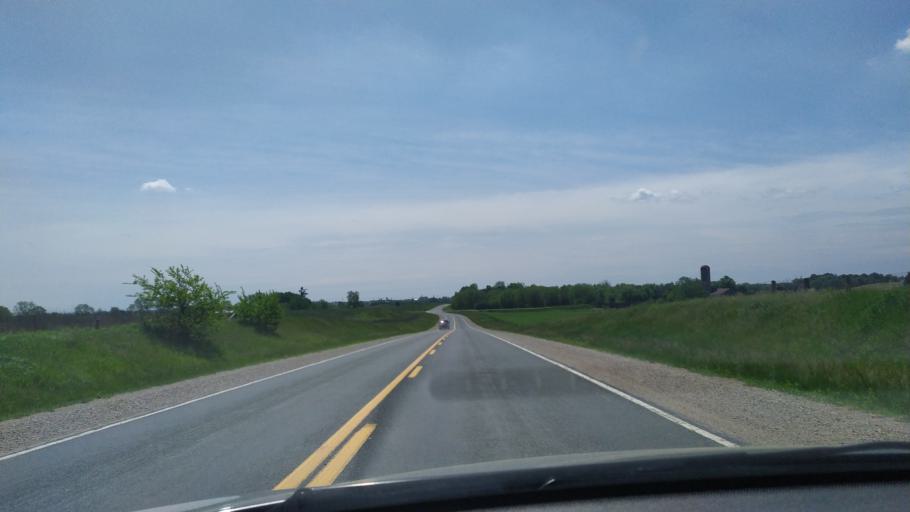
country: CA
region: Ontario
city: Ingersoll
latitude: 43.0186
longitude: -80.9671
